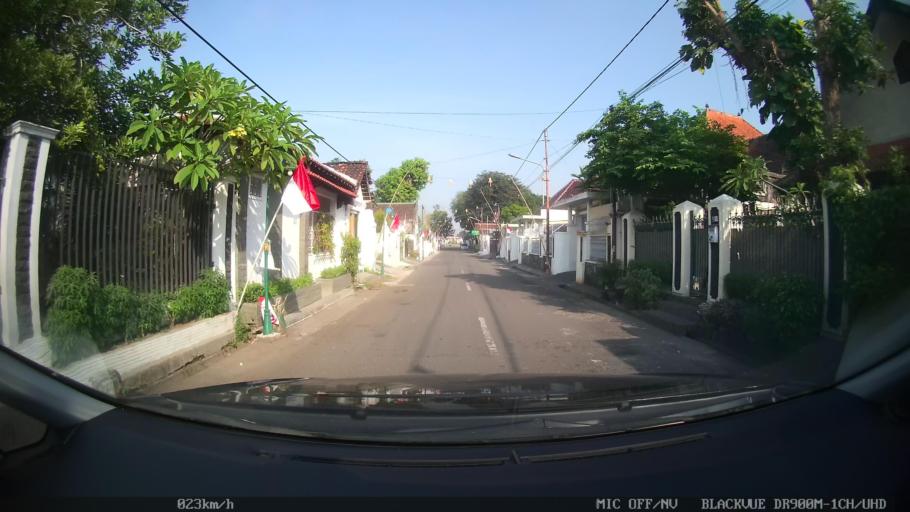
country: ID
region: Daerah Istimewa Yogyakarta
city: Yogyakarta
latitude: -7.8124
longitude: 110.3653
